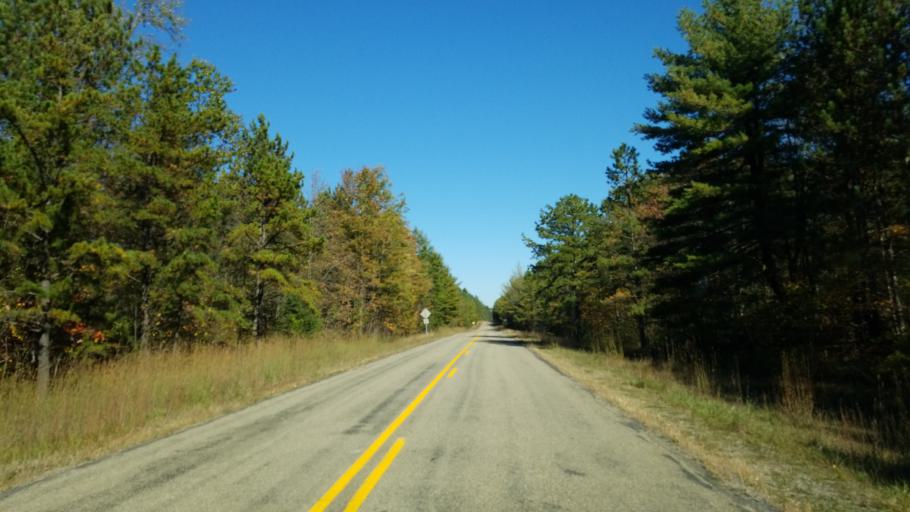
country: US
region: Pennsylvania
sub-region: Clearfield County
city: Shiloh
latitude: 41.2611
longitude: -78.2902
